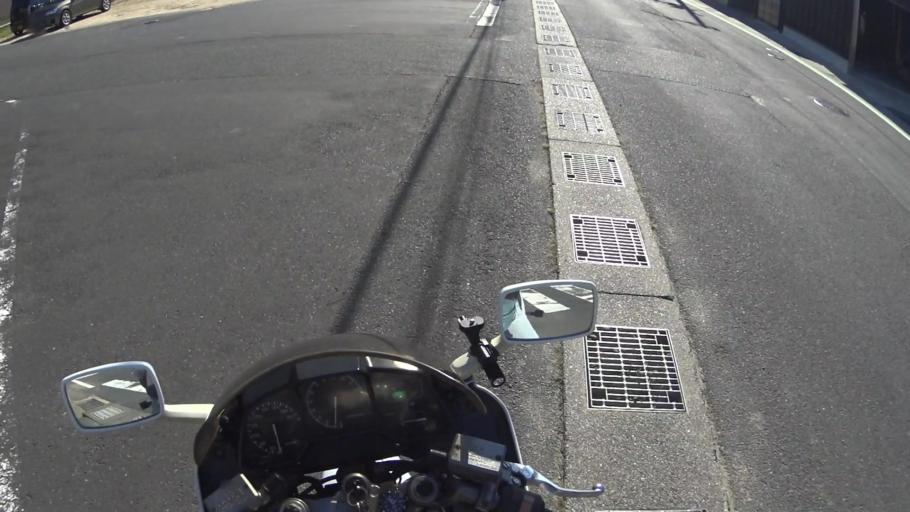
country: JP
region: Hyogo
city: Toyooka
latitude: 35.6309
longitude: 134.9280
